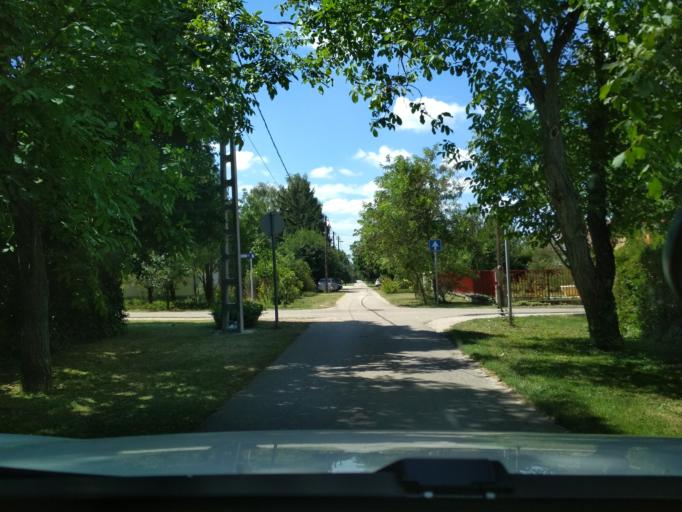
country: HU
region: Fejer
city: Gardony
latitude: 47.2121
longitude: 18.6546
